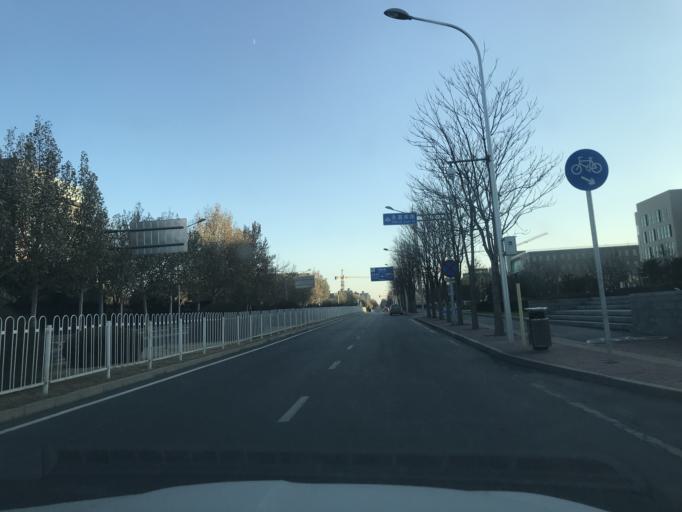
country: CN
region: Beijing
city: Xibeiwang
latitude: 40.0736
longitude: 116.2446
